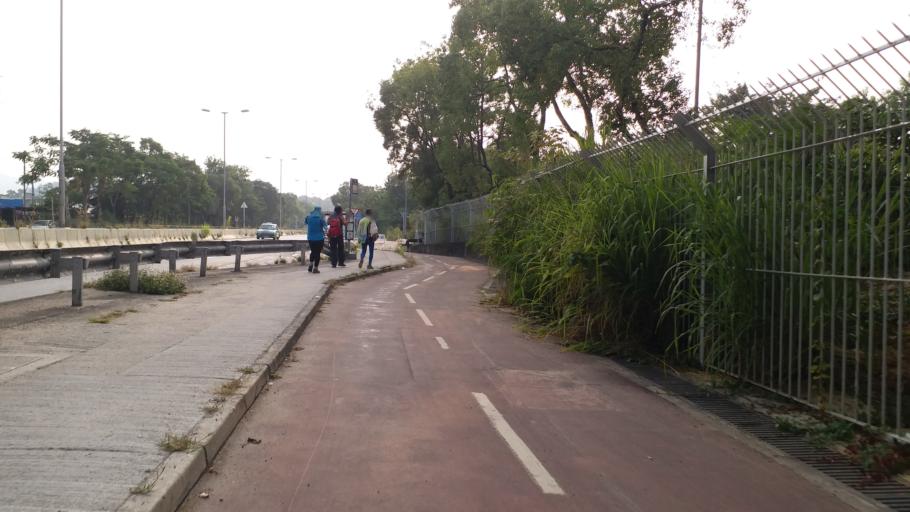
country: HK
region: Yuen Long
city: Yuen Long Kau Hui
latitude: 22.4486
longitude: 114.0188
